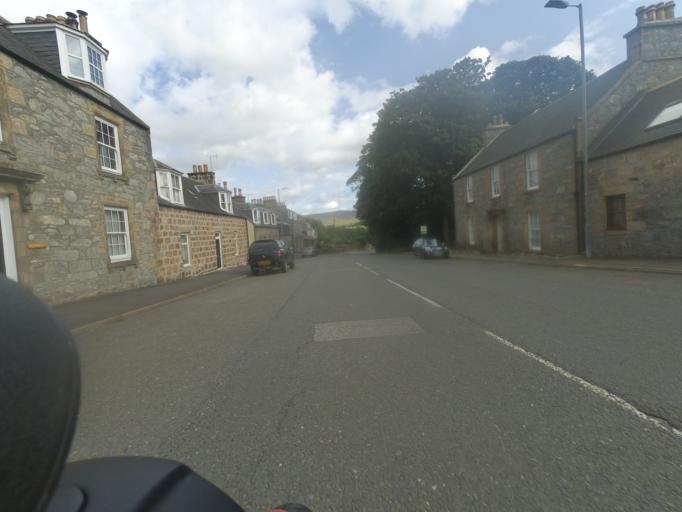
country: GB
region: Scotland
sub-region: Moray
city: Dufftown
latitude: 57.4447
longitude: -3.1248
